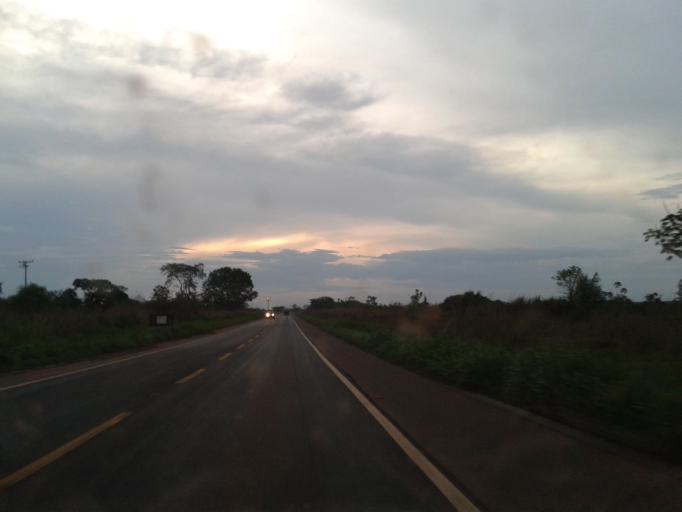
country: BR
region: Goias
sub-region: Santa Helena De Goias
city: Santa Helena de Goias
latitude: -17.8786
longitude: -50.7075
